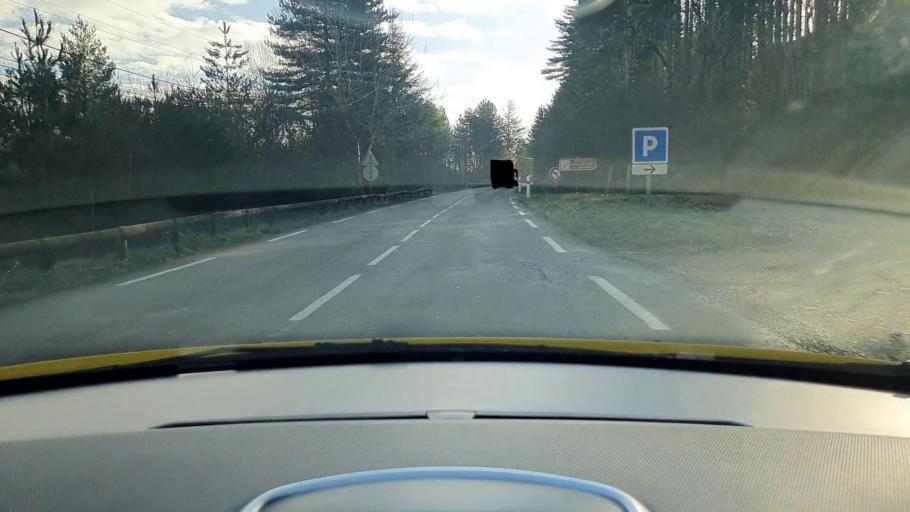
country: FR
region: Languedoc-Roussillon
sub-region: Departement du Gard
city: Branoux-les-Taillades
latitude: 44.3881
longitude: 3.9374
